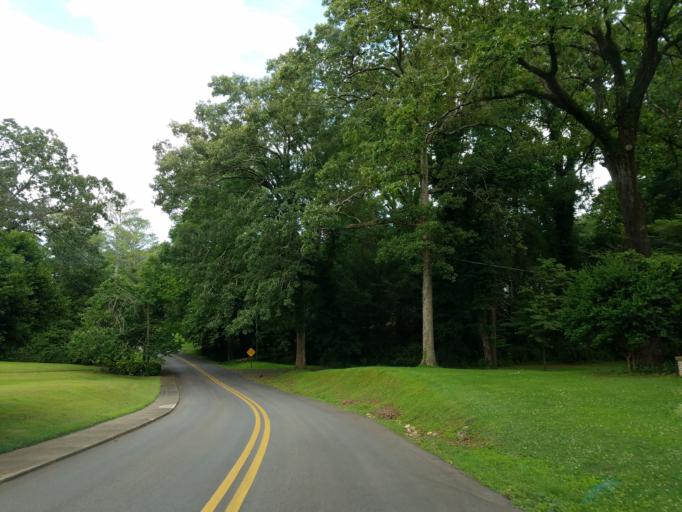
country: US
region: Georgia
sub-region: Pickens County
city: Nelson
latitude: 34.4190
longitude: -84.3852
